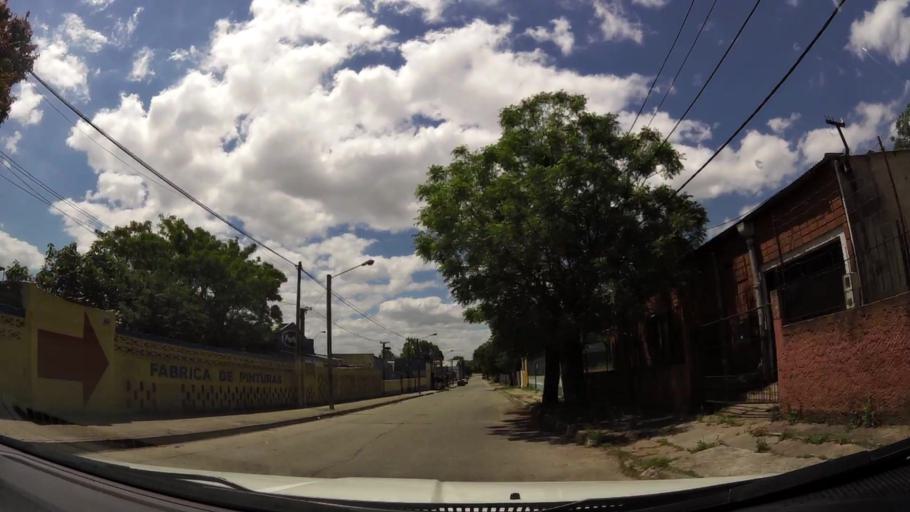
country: UY
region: Montevideo
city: Montevideo
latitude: -34.8525
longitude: -56.2381
